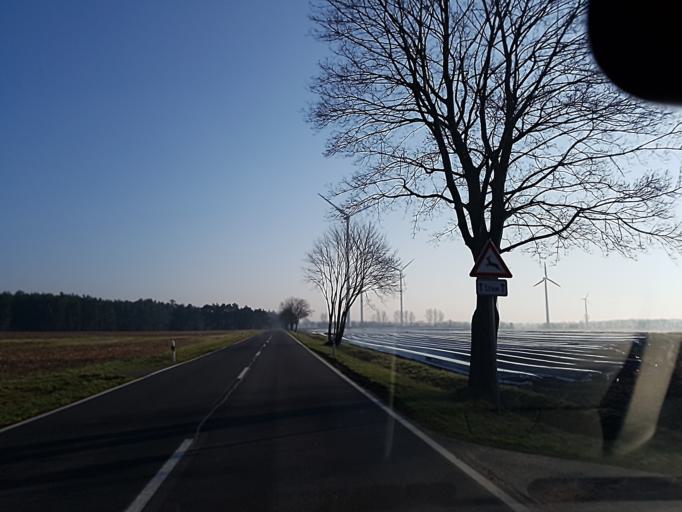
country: DE
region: Brandenburg
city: Sallgast
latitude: 51.6430
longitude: 13.8640
